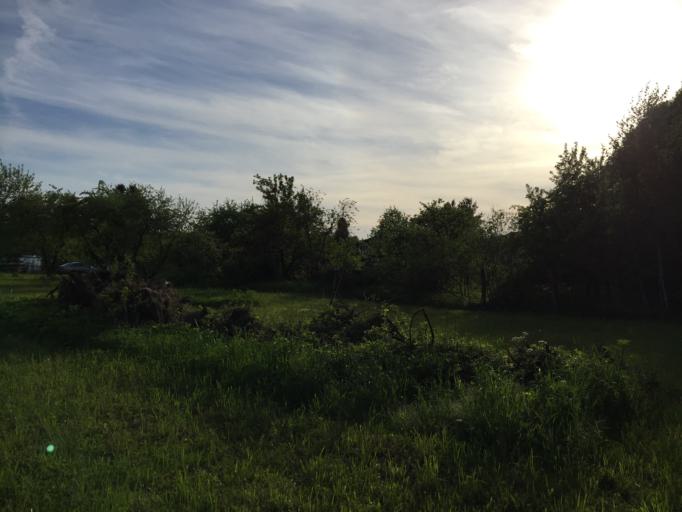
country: LV
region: Jelgava
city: Jelgava
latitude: 56.6355
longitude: 23.6827
